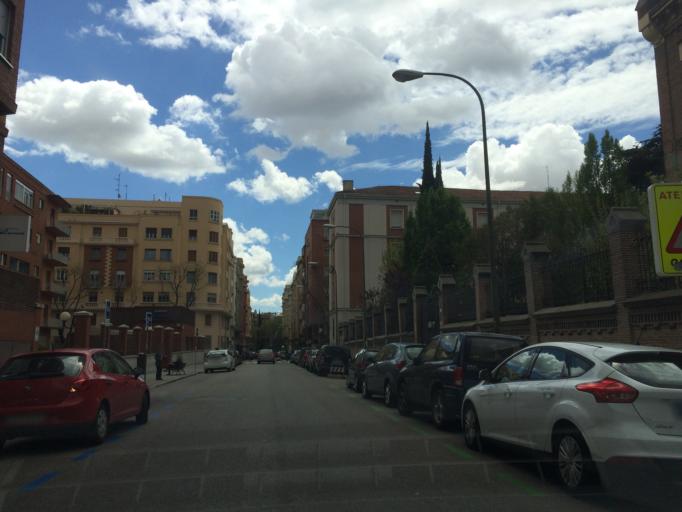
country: ES
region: Madrid
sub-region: Provincia de Madrid
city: Chamberi
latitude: 40.4374
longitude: -3.6964
